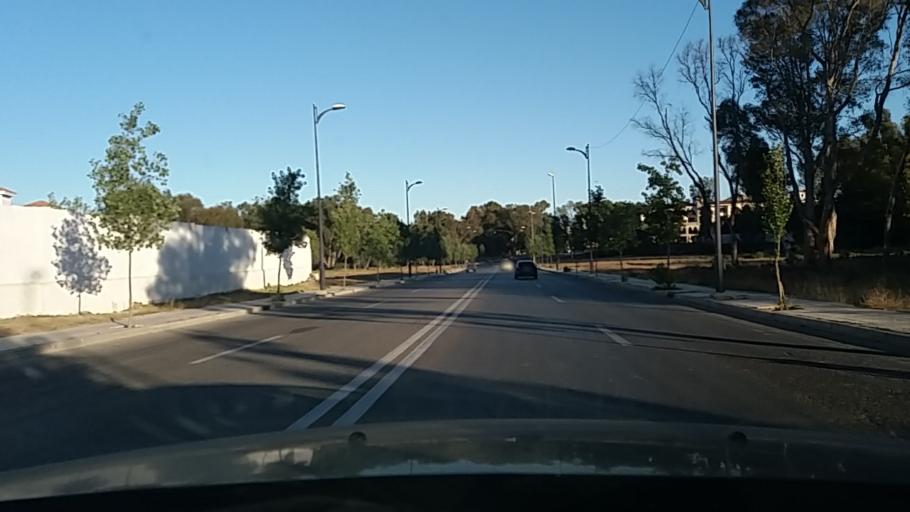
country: MA
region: Tanger-Tetouan
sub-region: Tanger-Assilah
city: Tangier
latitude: 35.7754
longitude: -5.8584
